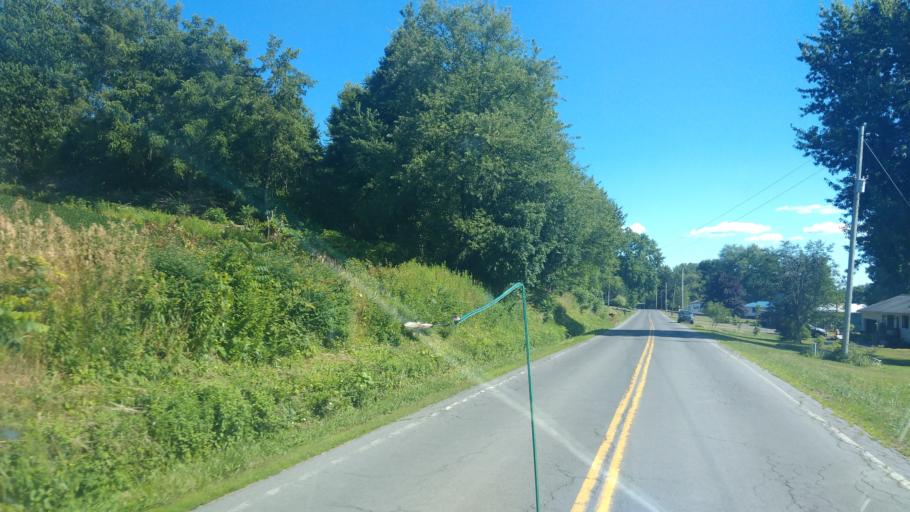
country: US
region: New York
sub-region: Wayne County
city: Clyde
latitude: 43.0127
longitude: -76.8113
